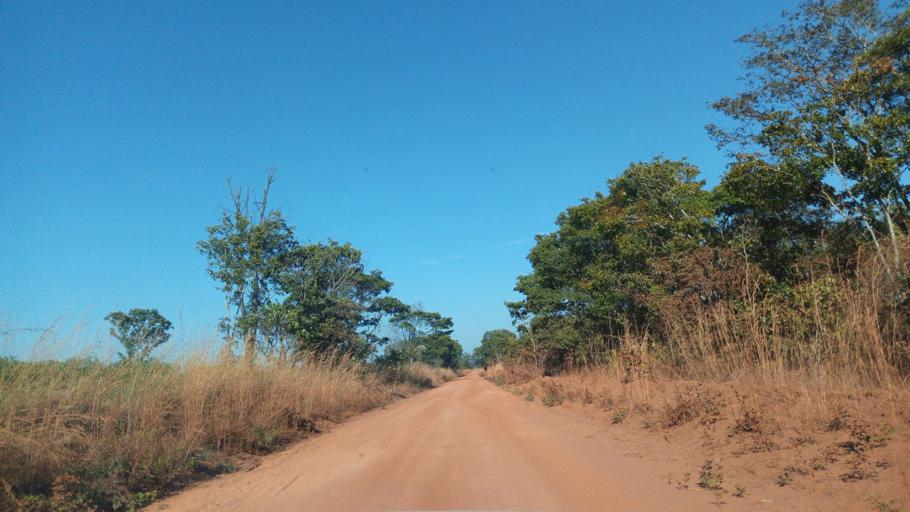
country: ZM
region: Luapula
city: Mwense
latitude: -10.5987
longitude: 28.4273
